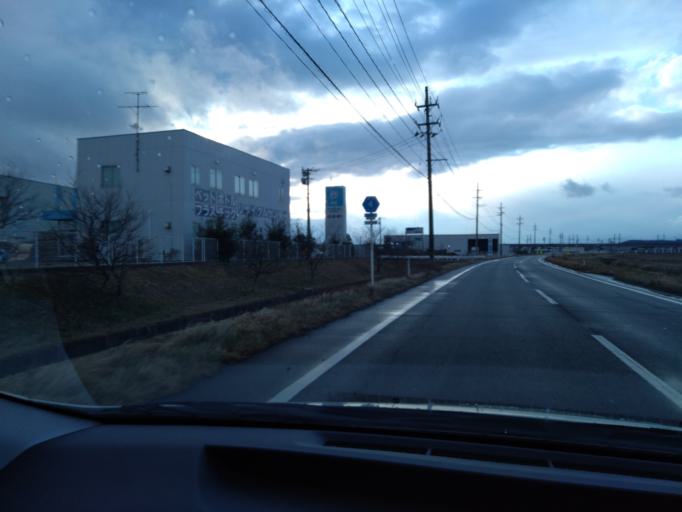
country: JP
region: Iwate
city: Ichinoseki
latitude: 38.7888
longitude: 141.0993
